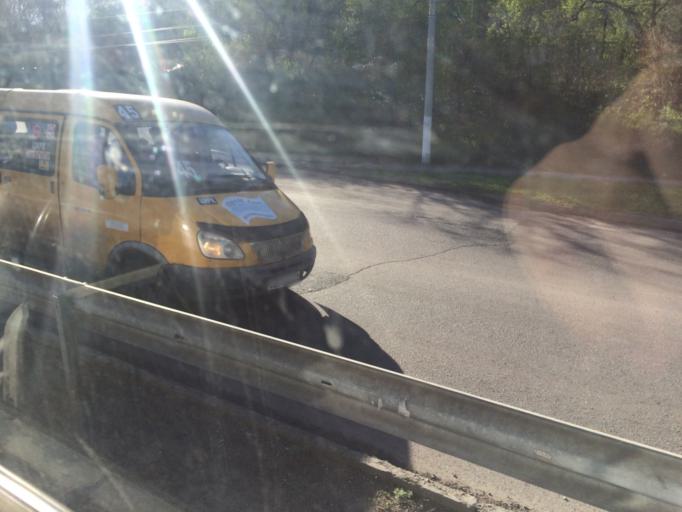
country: RU
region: Chelyabinsk
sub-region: Gorod Magnitogorsk
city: Magnitogorsk
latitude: 53.4024
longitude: 59.0451
